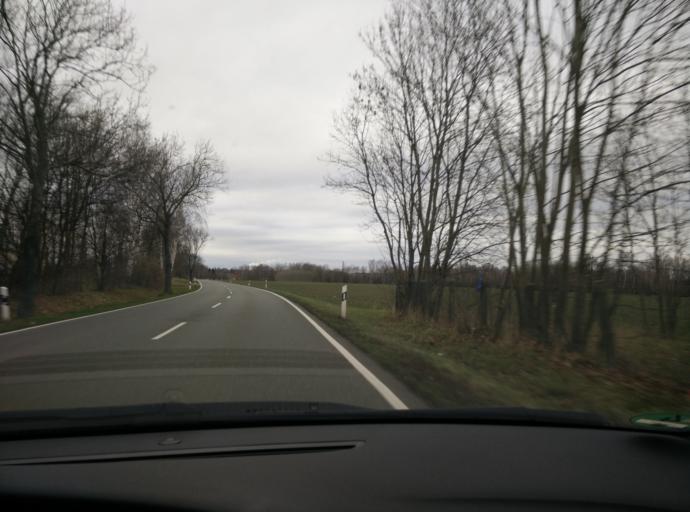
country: DE
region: Saxony
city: Frohburg
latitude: 51.0712
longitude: 12.5522
